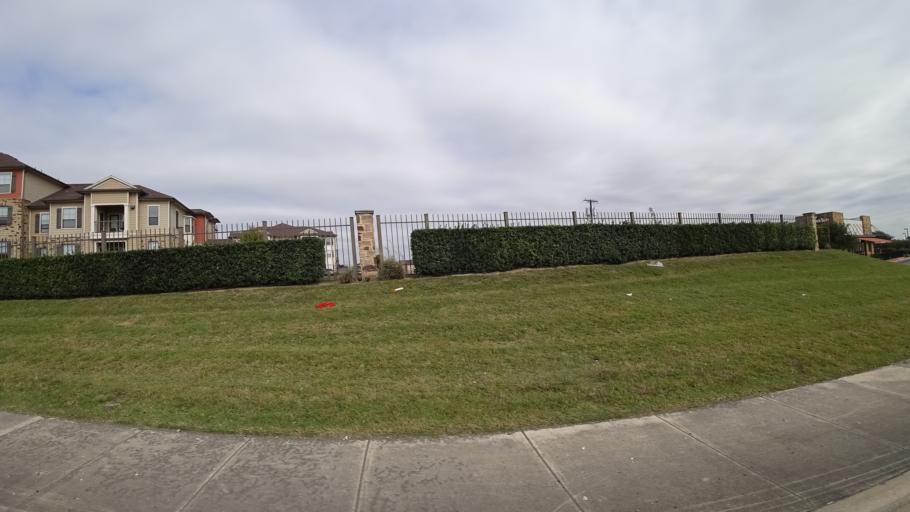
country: US
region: Texas
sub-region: Travis County
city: Windemere
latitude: 30.4560
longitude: -97.6619
